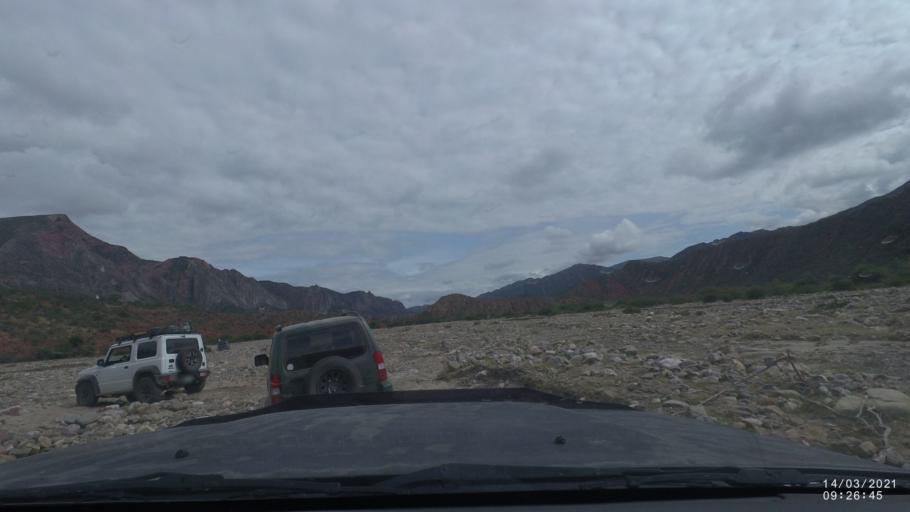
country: BO
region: Cochabamba
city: Cliza
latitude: -17.9478
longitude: -65.8559
